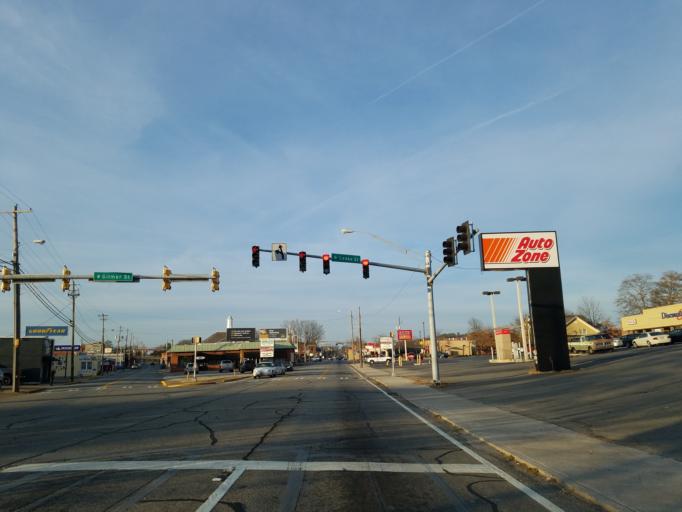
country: US
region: Georgia
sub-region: Bartow County
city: Cartersville
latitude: 34.1639
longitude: -84.7936
